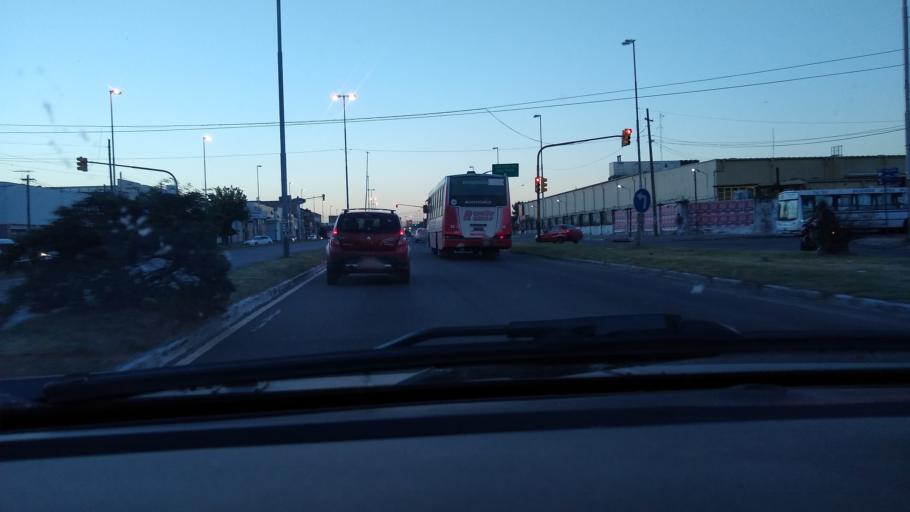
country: AR
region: Buenos Aires
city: San Justo
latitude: -34.6897
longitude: -58.5550
